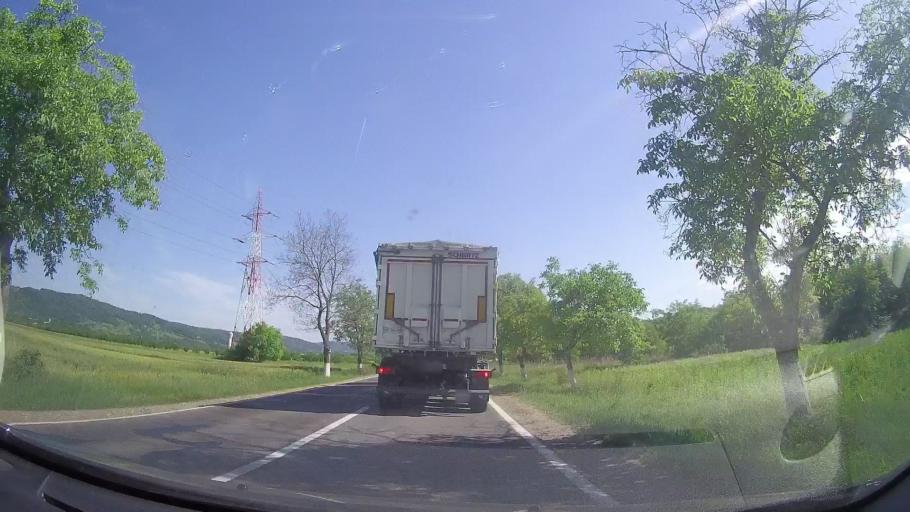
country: RO
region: Prahova
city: Drajna de Jos
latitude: 45.2312
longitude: 26.0301
